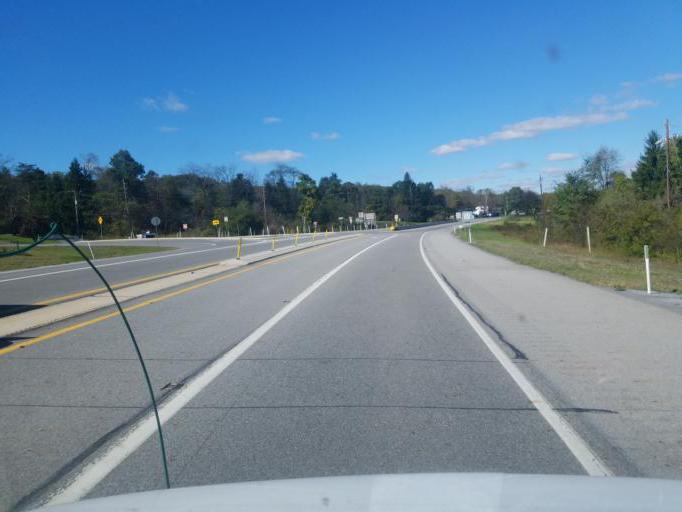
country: US
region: Pennsylvania
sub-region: Bedford County
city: Bedford
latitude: 40.0363
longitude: -78.5219
